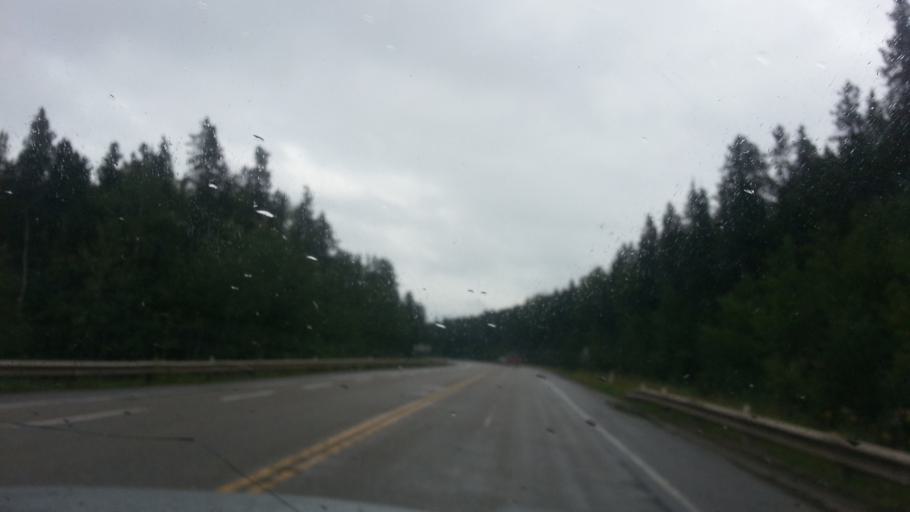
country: CA
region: Alberta
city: Cochrane
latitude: 50.9115
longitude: -114.6386
